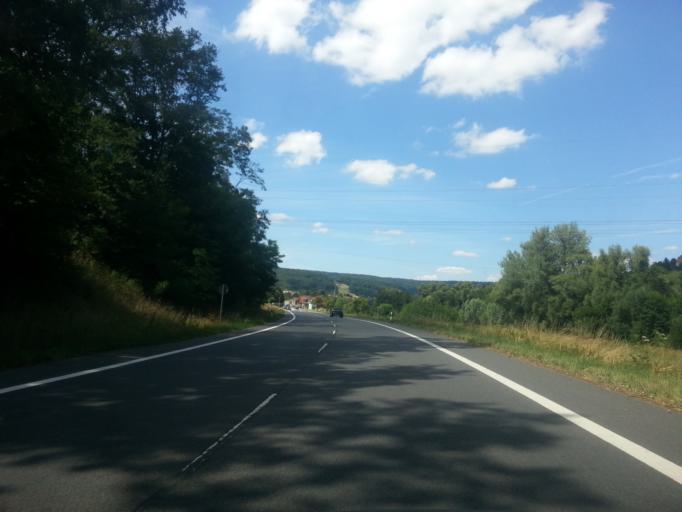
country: DE
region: Hesse
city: Reichelsheim
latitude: 49.7077
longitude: 8.8527
